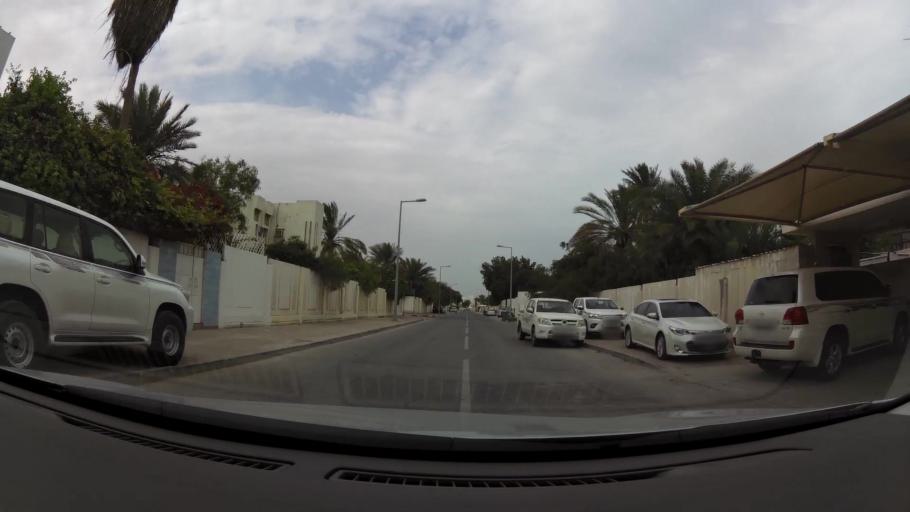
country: QA
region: Baladiyat ad Dawhah
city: Doha
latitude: 25.3322
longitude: 51.5053
